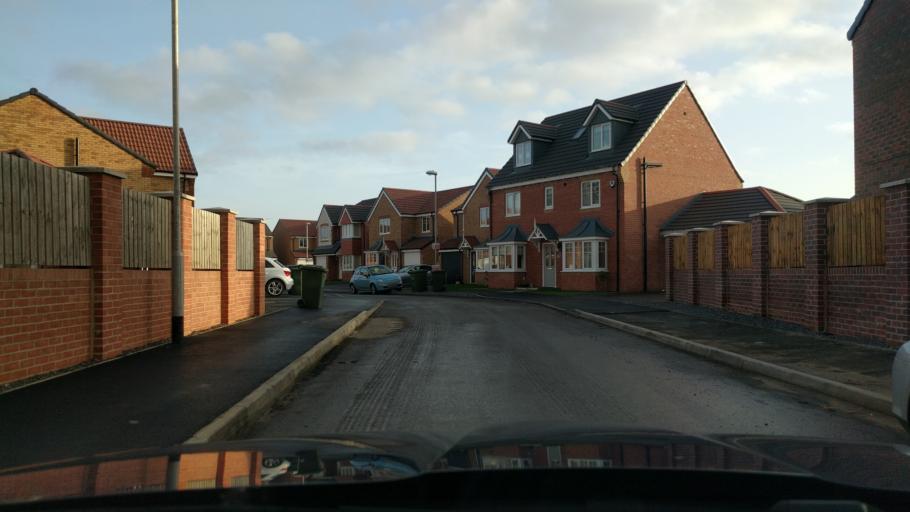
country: GB
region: England
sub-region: Northumberland
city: Ashington
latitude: 55.1866
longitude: -1.5926
